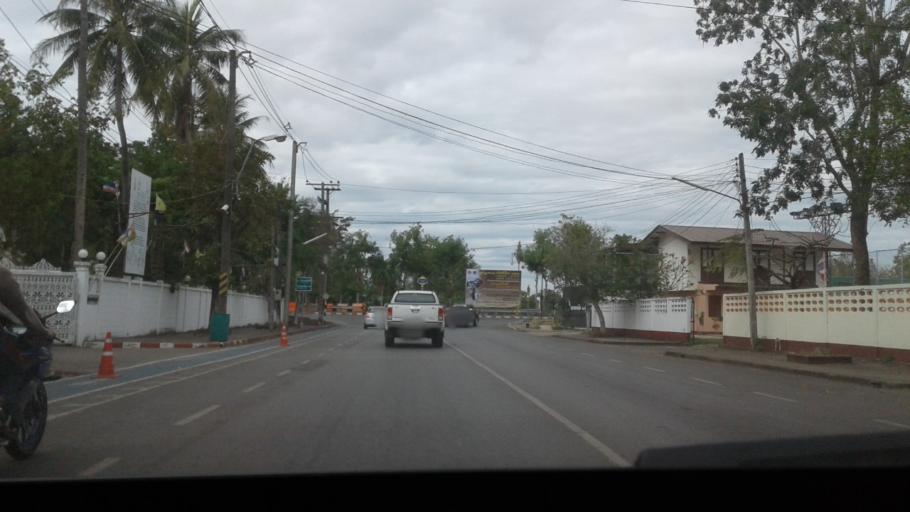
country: TH
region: Changwat Udon Thani
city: Udon Thani
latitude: 17.4165
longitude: 102.7864
